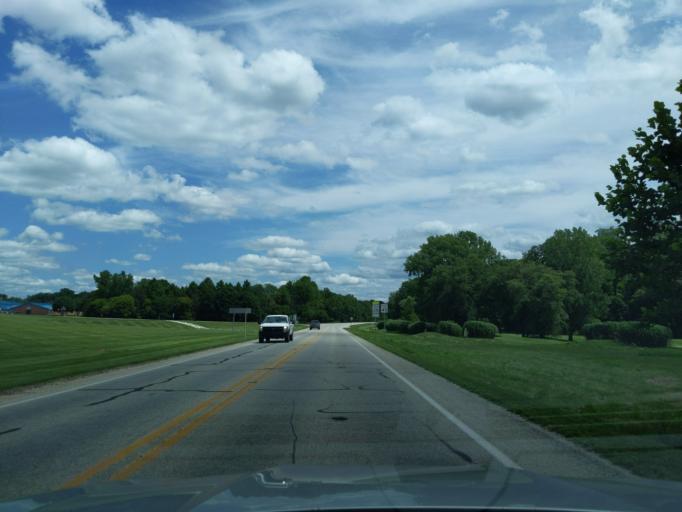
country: US
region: Indiana
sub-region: Ripley County
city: Batesville
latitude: 39.3091
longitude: -85.2345
